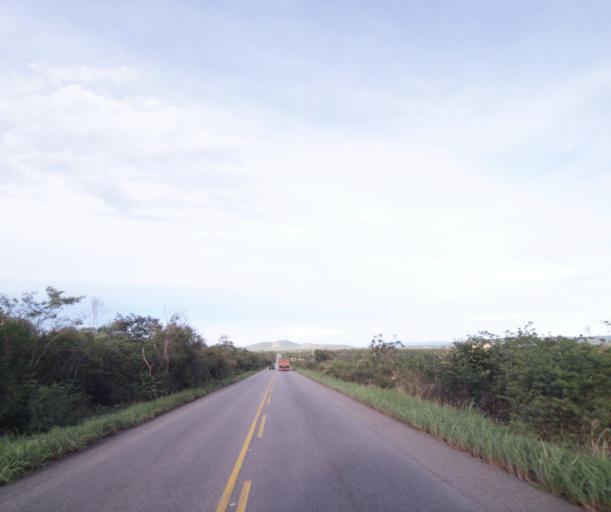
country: BR
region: Bahia
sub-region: Caetite
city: Caetite
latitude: -14.1722
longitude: -42.2781
